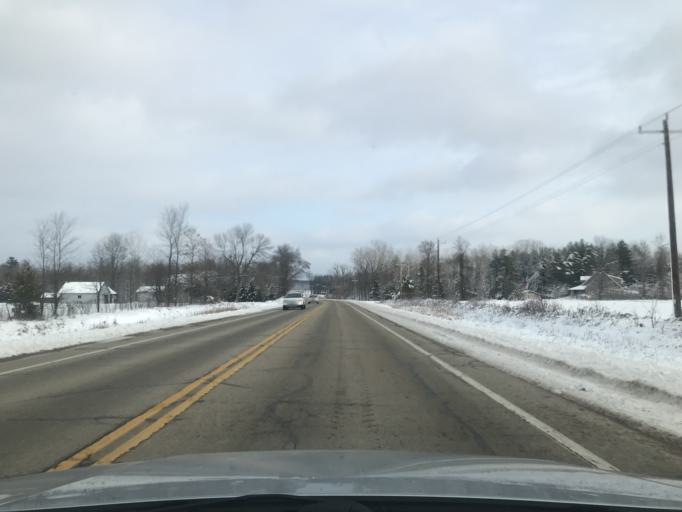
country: US
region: Wisconsin
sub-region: Oconto County
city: Oconto Falls
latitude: 44.8875
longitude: -88.0183
